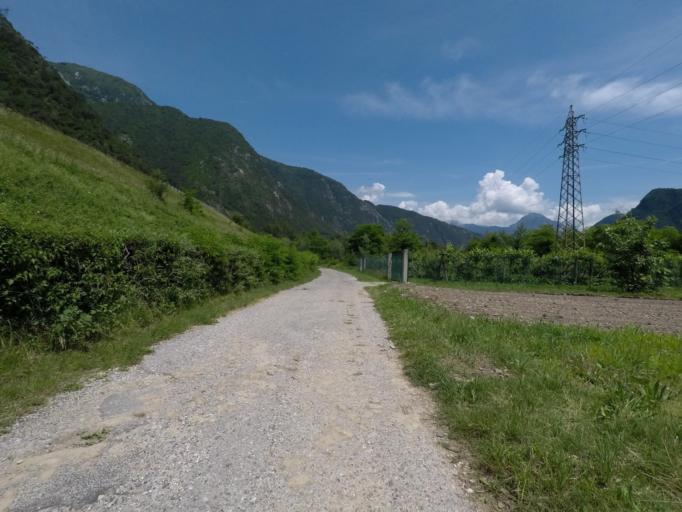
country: IT
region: Friuli Venezia Giulia
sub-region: Provincia di Udine
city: Amaro
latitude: 46.3798
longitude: 13.1179
